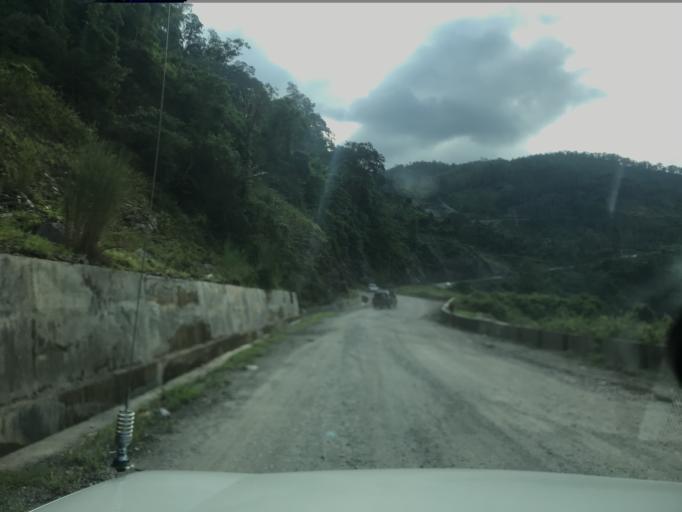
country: TL
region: Aileu
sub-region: Aileu Villa
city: Aileu
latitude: -8.6434
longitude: 125.5200
